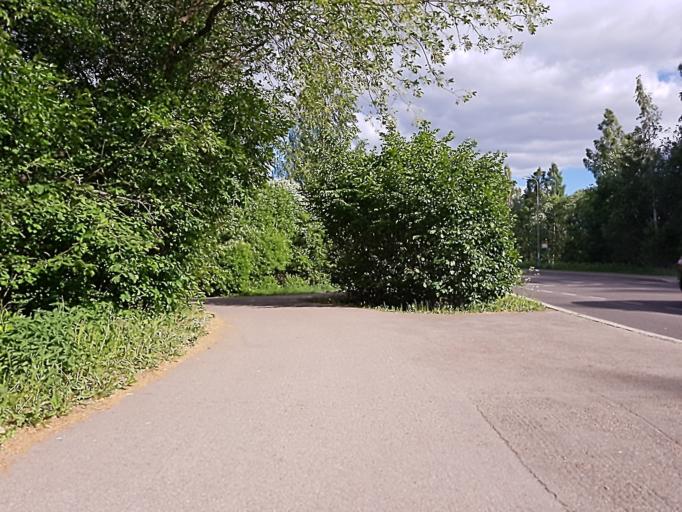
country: FI
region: Uusimaa
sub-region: Helsinki
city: Teekkarikylae
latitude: 60.2433
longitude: 24.8542
